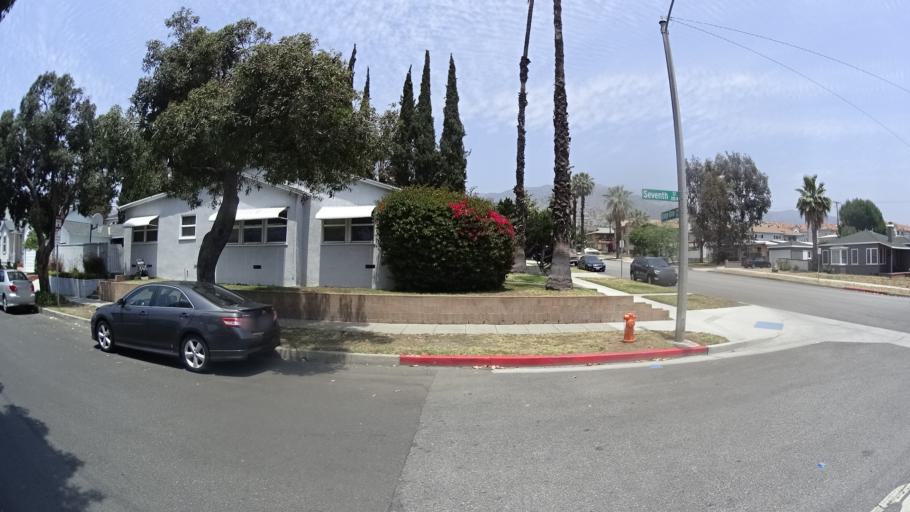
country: US
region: California
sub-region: Los Angeles County
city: Burbank
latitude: 34.1875
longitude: -118.3038
